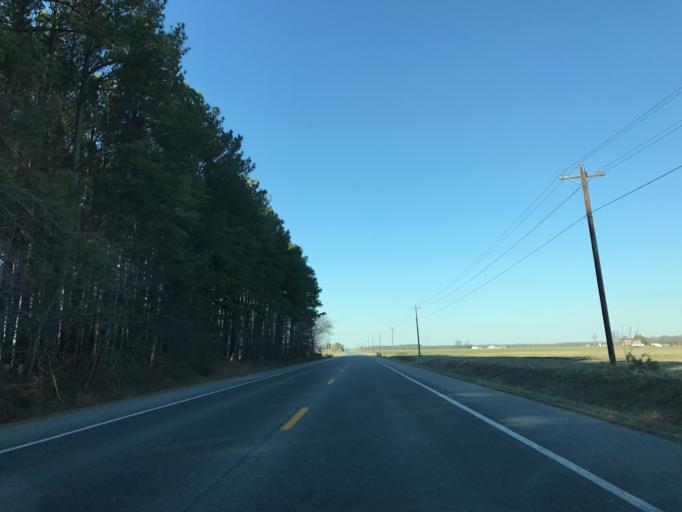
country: US
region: Maryland
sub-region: Caroline County
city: Greensboro
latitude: 39.1057
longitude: -75.8731
